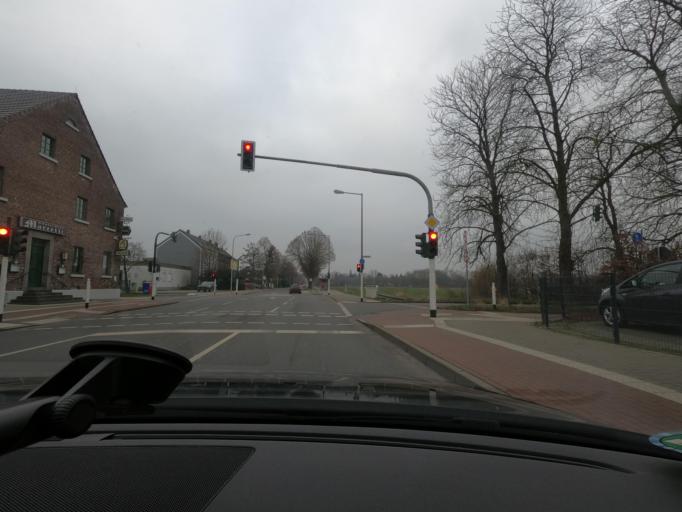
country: DE
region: North Rhine-Westphalia
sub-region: Regierungsbezirk Dusseldorf
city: Krefeld
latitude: 51.3617
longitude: 6.5704
